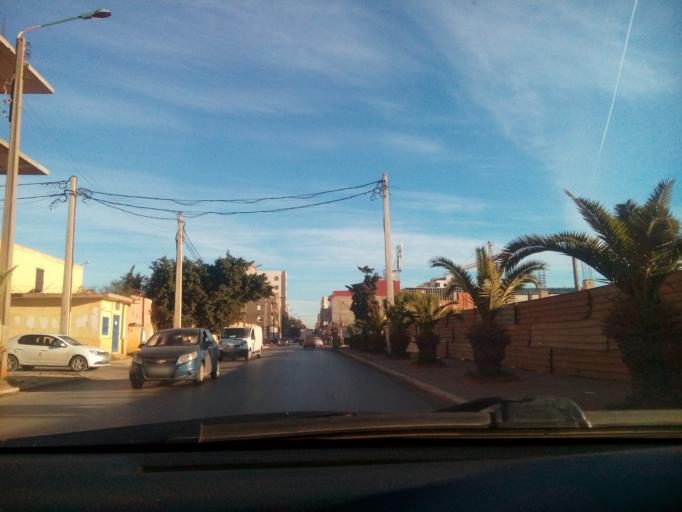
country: DZ
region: Oran
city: Oran
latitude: 35.6771
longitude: -0.6615
